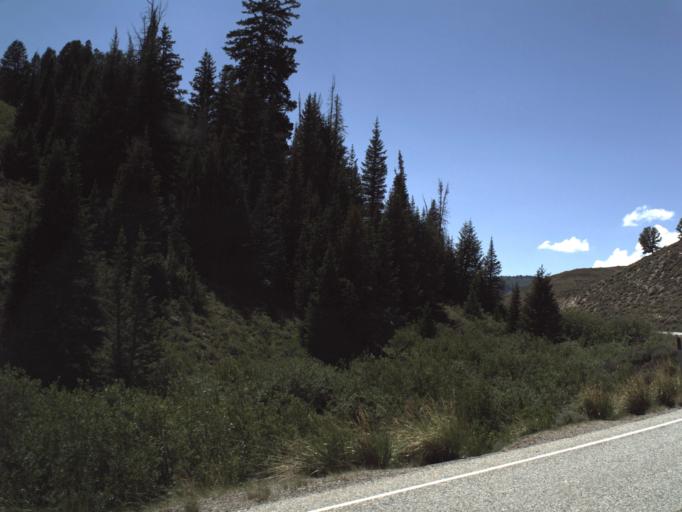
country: US
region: Utah
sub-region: Rich County
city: Randolph
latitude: 41.4828
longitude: -111.3909
